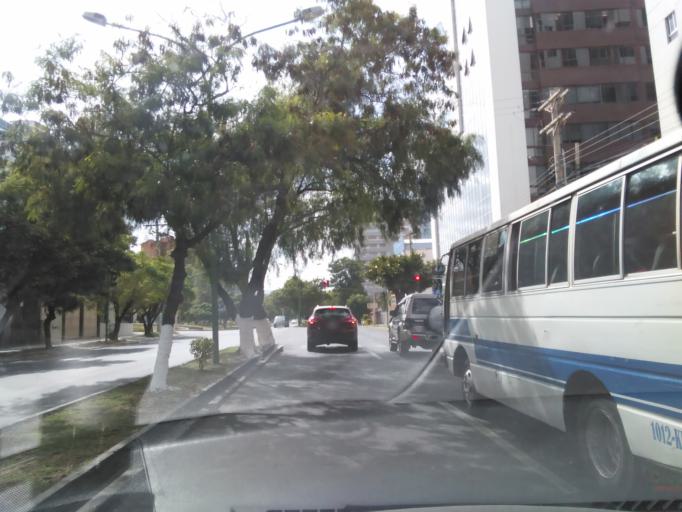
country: BO
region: Cochabamba
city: Cochabamba
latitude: -17.3735
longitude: -66.1474
